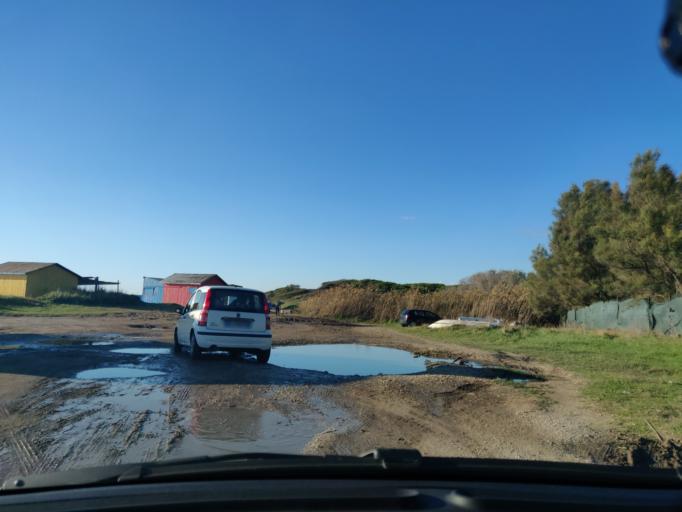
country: IT
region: Latium
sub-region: Citta metropolitana di Roma Capitale
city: Aurelia
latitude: 42.1494
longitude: 11.7437
